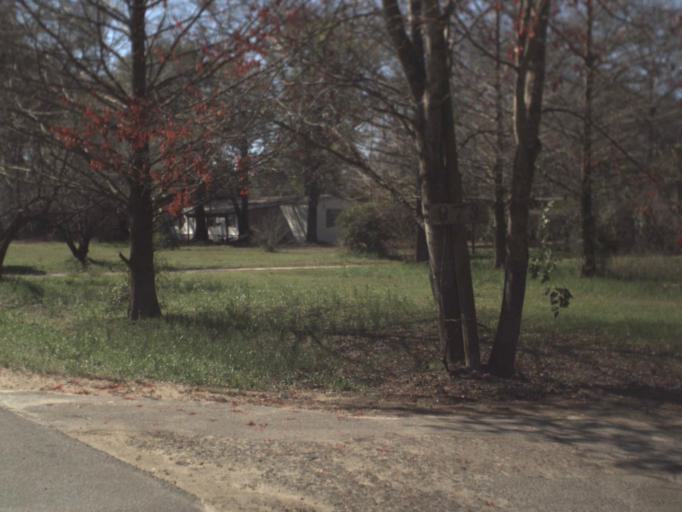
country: US
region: Florida
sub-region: Jackson County
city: Marianna
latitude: 30.6349
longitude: -85.1573
